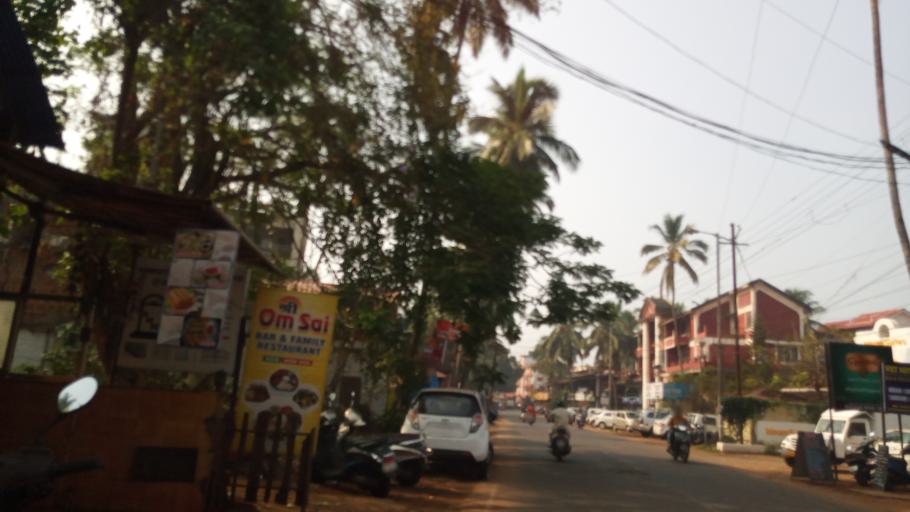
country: IN
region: Goa
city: Calangute
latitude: 15.5403
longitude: 73.7647
